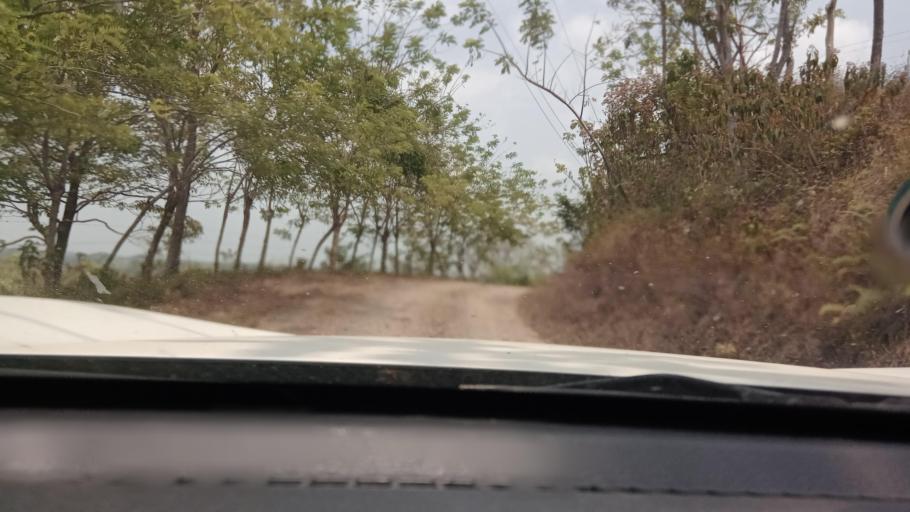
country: MX
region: Tabasco
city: Chontalpa
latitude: 17.5583
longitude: -93.7209
